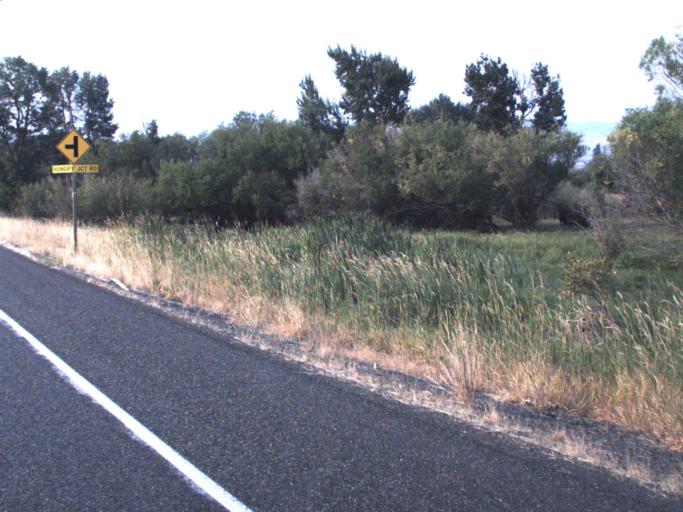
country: US
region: Washington
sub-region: Kittitas County
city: Ellensburg
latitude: 47.0456
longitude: -120.6086
